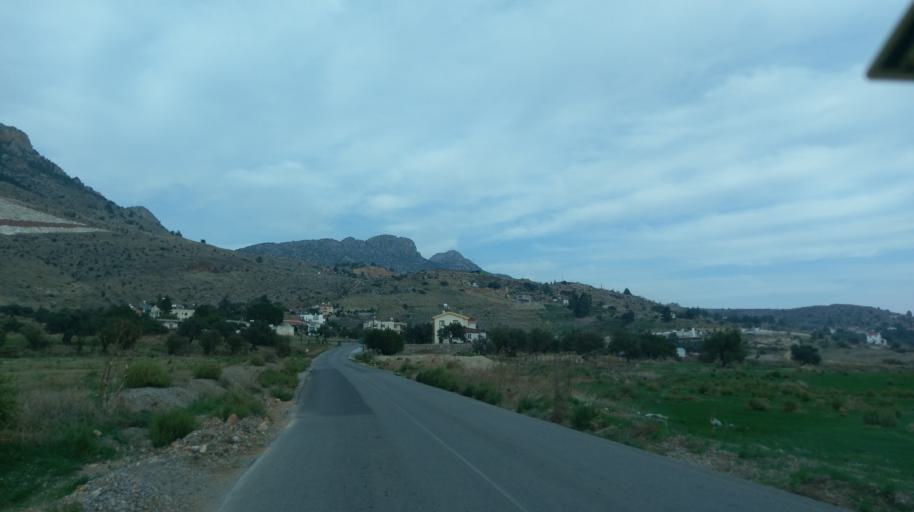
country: CY
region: Keryneia
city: Kyrenia
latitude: 35.2759
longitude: 33.3734
